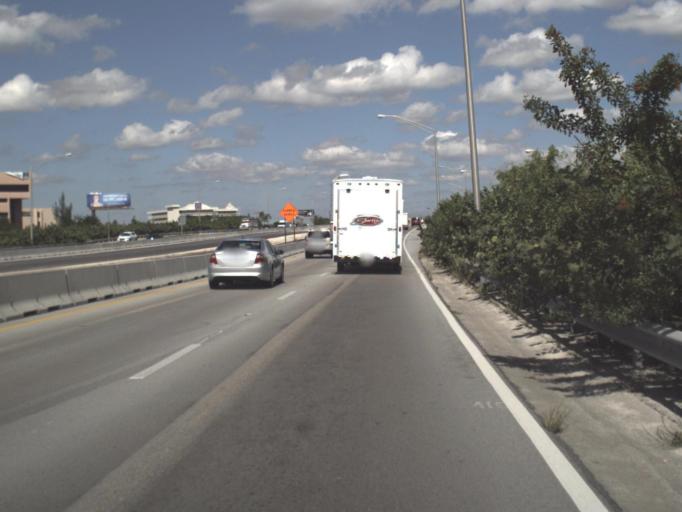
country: US
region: Florida
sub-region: Miami-Dade County
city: Cutler Ridge
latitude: 25.5745
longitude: -80.3638
